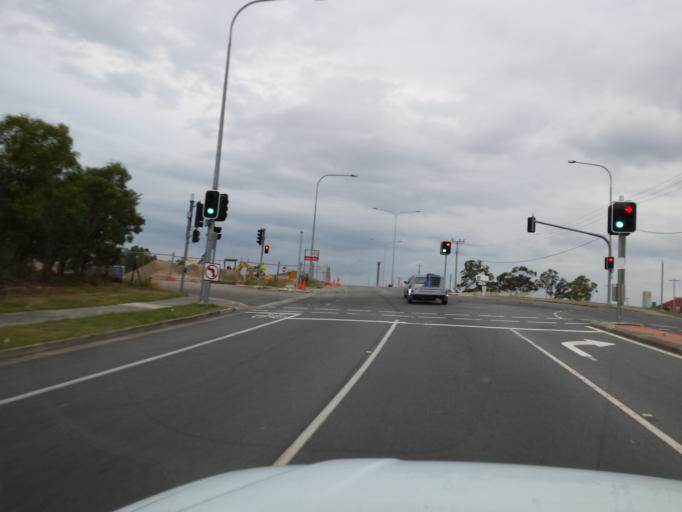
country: AU
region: Queensland
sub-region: Gold Coast
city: Oxenford
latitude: -27.8571
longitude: 153.3049
